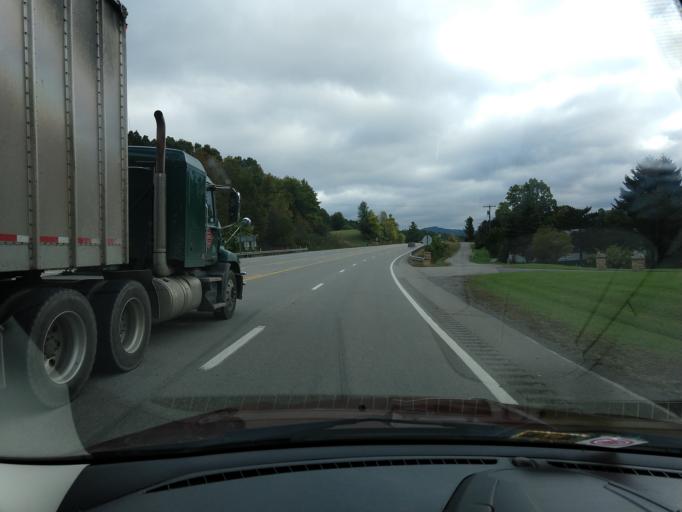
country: US
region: West Virginia
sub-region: Randolph County
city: Elkins
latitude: 38.8637
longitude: -79.8551
